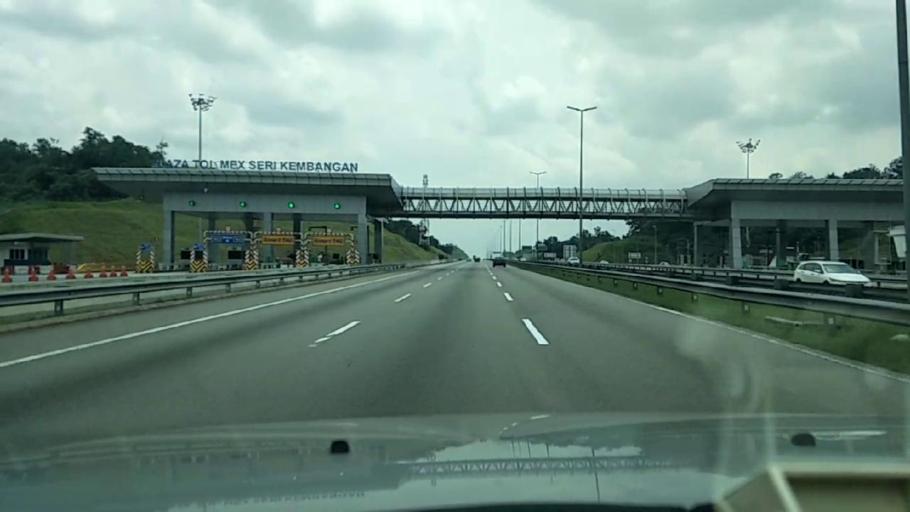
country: MY
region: Selangor
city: Kampong Baharu Balakong
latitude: 3.0163
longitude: 101.6835
